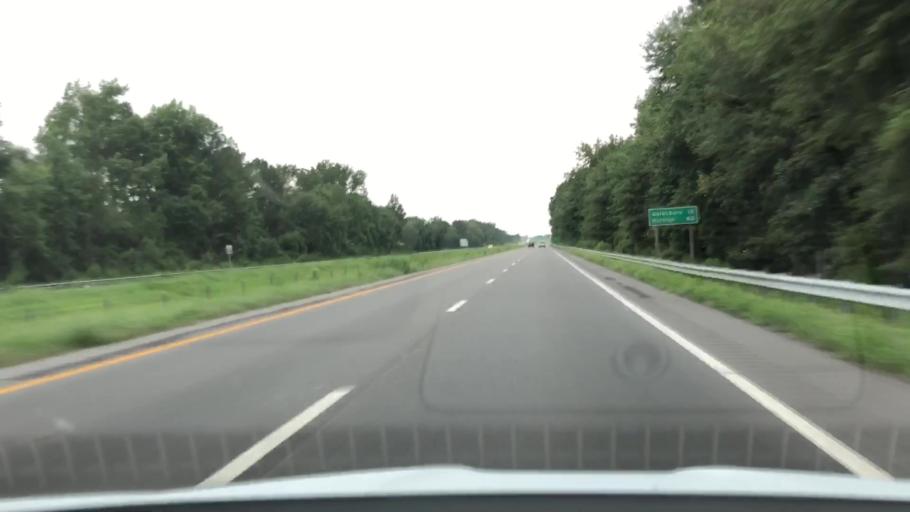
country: US
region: North Carolina
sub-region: Lenoir County
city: La Grange
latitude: 35.2938
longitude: -77.8022
